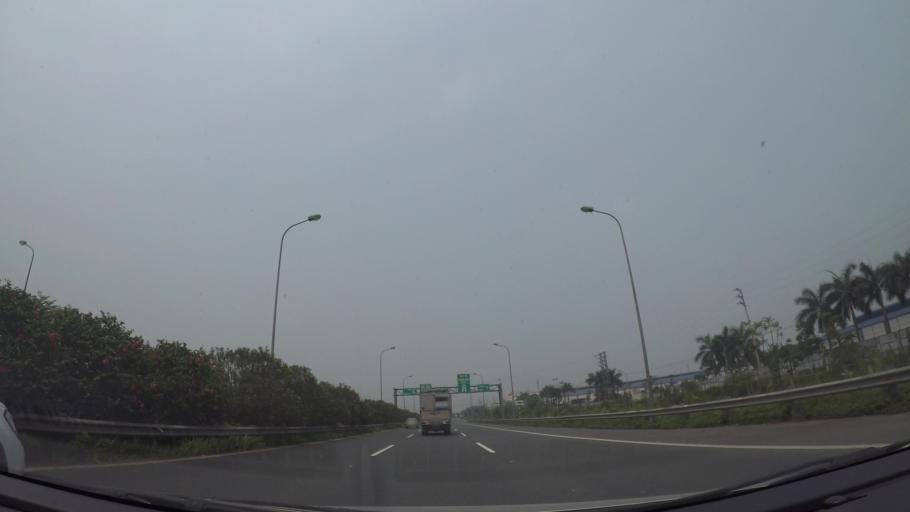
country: VN
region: Ha Noi
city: Quoc Oai
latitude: 21.0031
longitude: 105.6338
